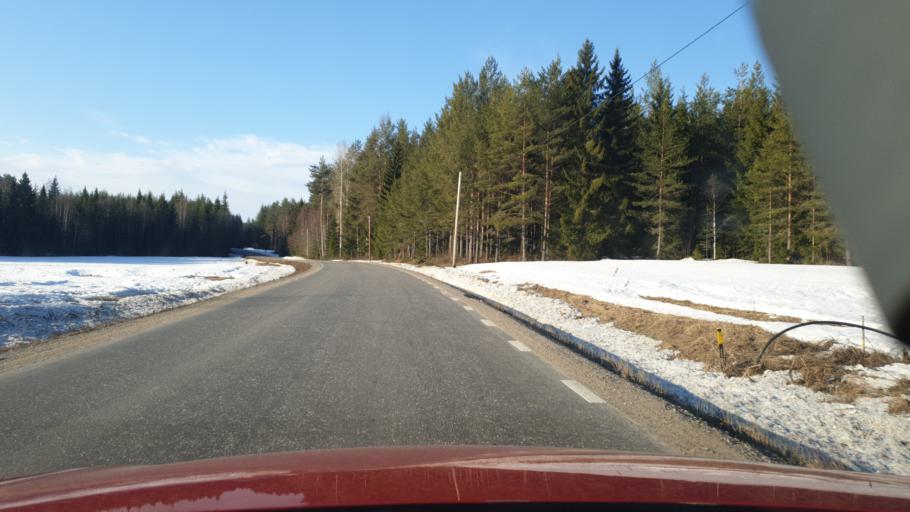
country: SE
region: Gaevleborg
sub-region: Ljusdals Kommun
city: Jaervsoe
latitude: 61.7663
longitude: 16.2102
